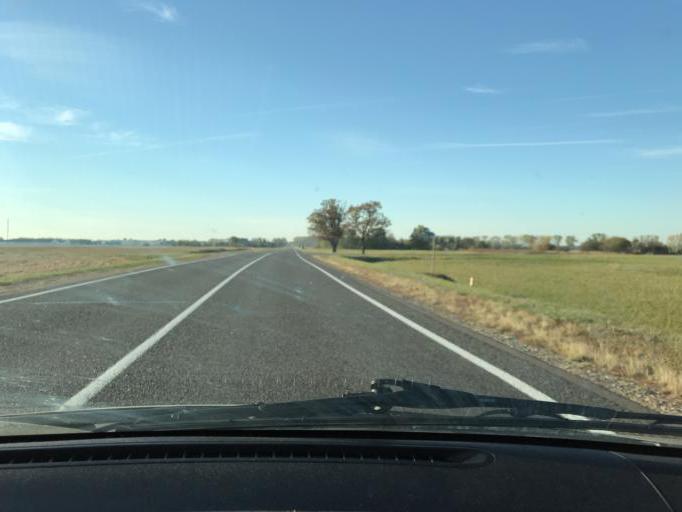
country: BY
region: Brest
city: Horad Kobryn
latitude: 52.2111
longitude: 24.4662
